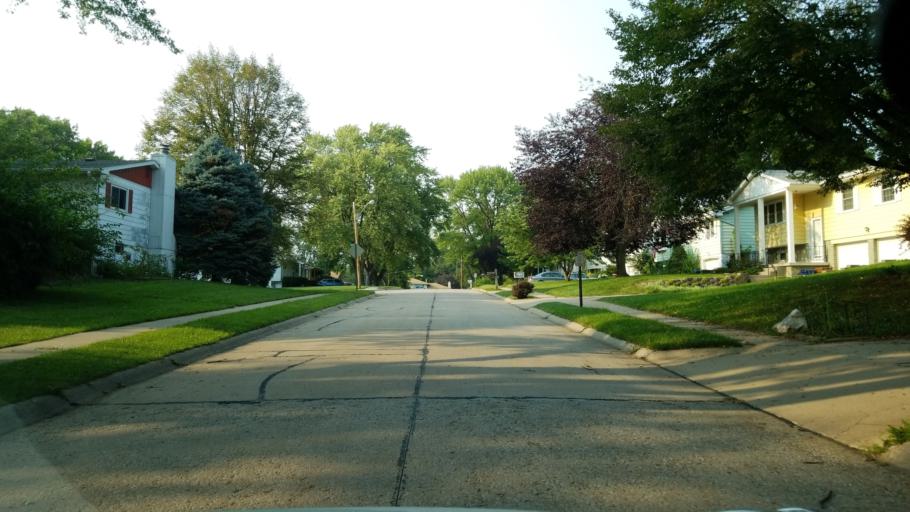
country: US
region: Nebraska
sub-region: Sarpy County
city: Bellevue
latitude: 41.1250
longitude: -95.8988
